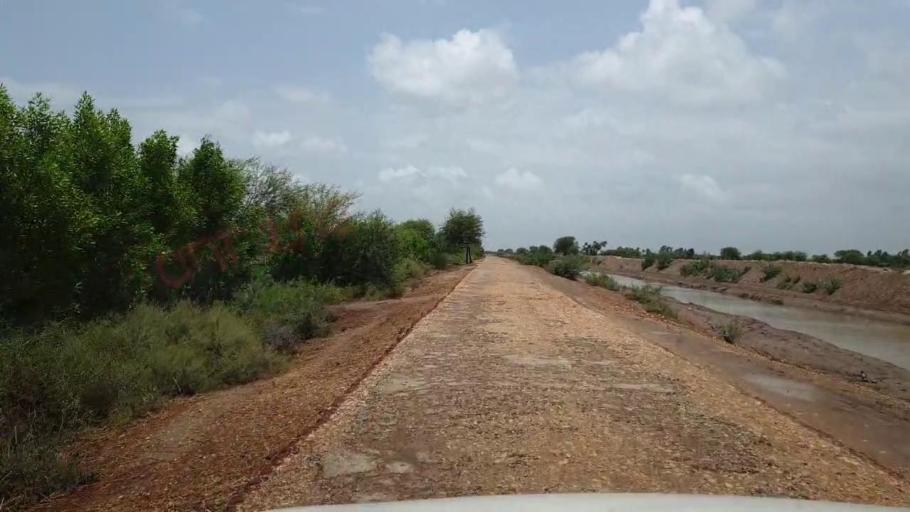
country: PK
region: Sindh
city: Kario
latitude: 24.7130
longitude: 68.5921
